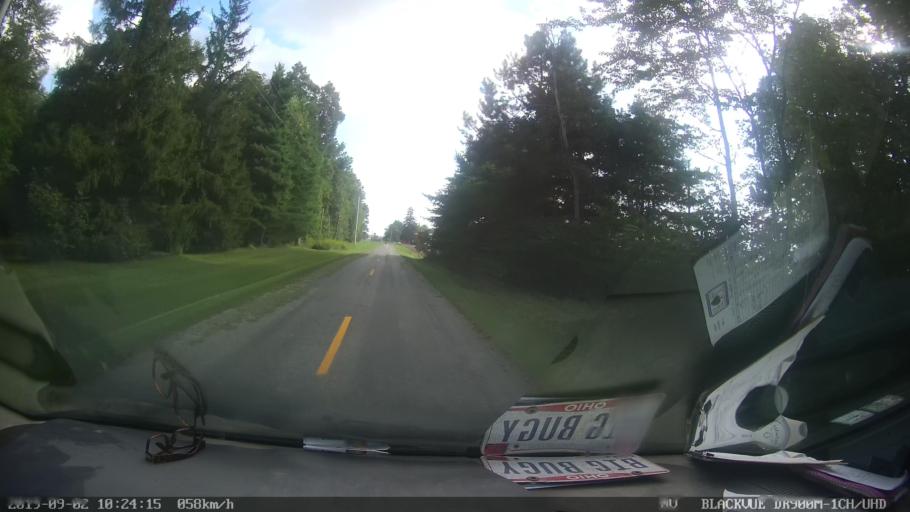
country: US
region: Ohio
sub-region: Delaware County
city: Ashley
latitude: 40.4938
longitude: -82.9958
